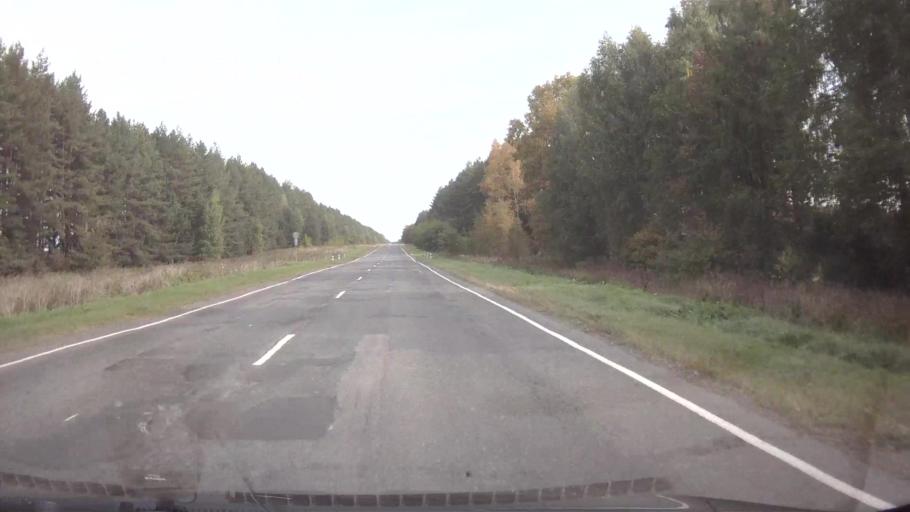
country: RU
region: Mariy-El
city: Kuzhener
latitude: 56.8251
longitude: 48.7222
